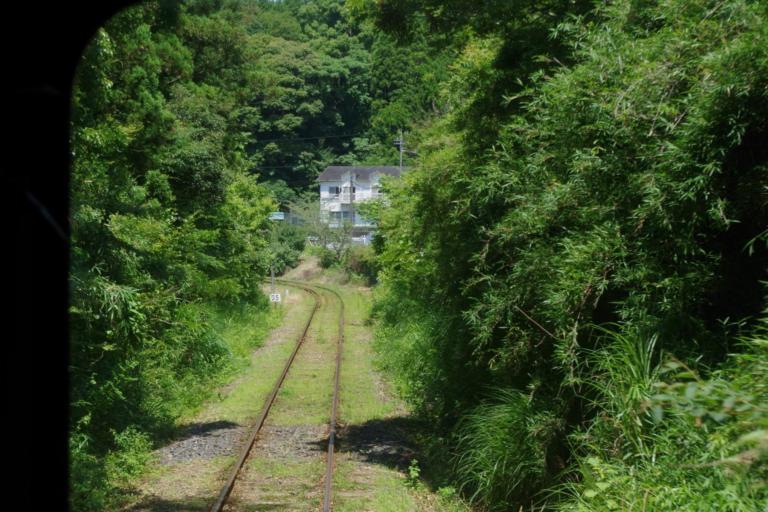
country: JP
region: Chiba
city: Katsuura
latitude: 35.2493
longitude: 140.2079
